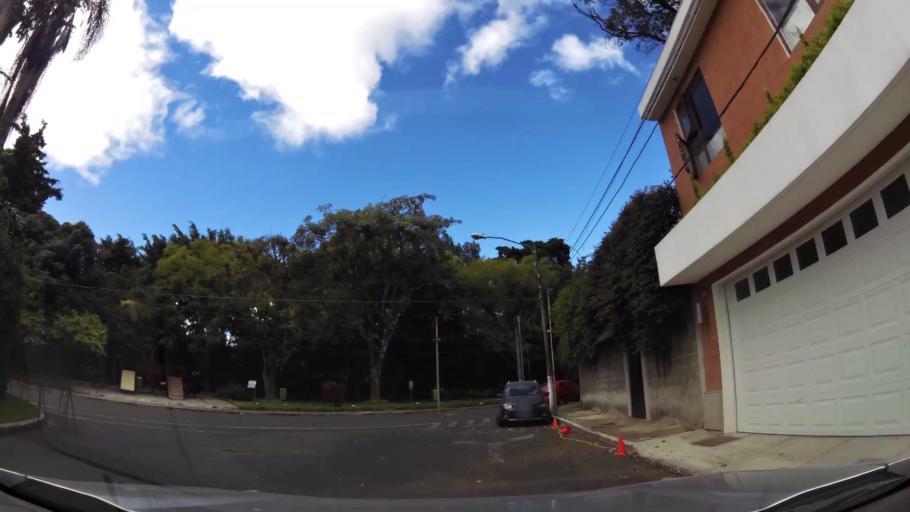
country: GT
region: Guatemala
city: Guatemala City
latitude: 14.6096
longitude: -90.5084
